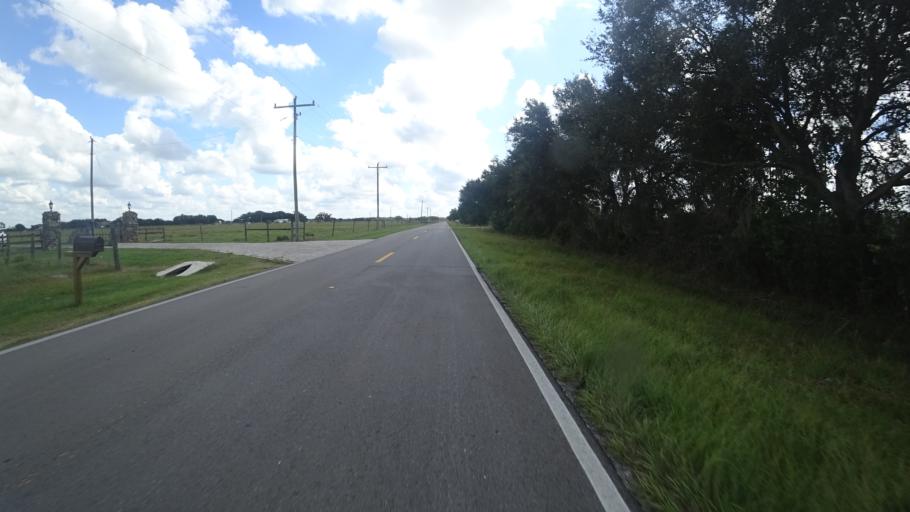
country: US
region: Florida
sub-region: Sarasota County
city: Warm Mineral Springs
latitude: 27.2800
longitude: -82.2120
